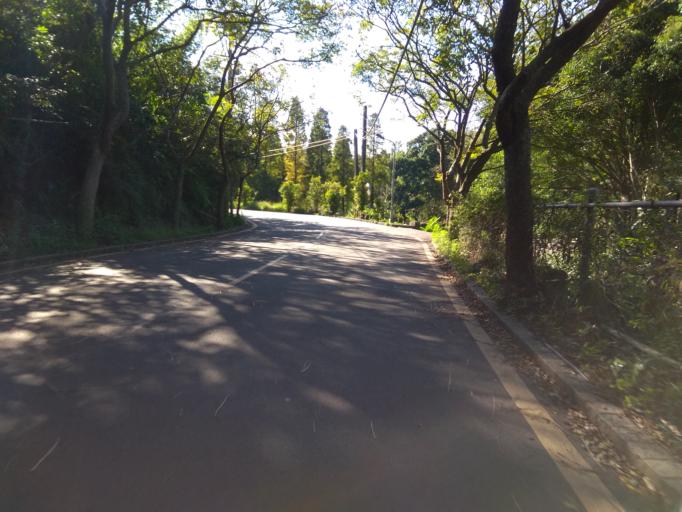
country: TW
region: Taiwan
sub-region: Hsinchu
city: Zhubei
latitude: 24.8597
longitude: 121.1048
